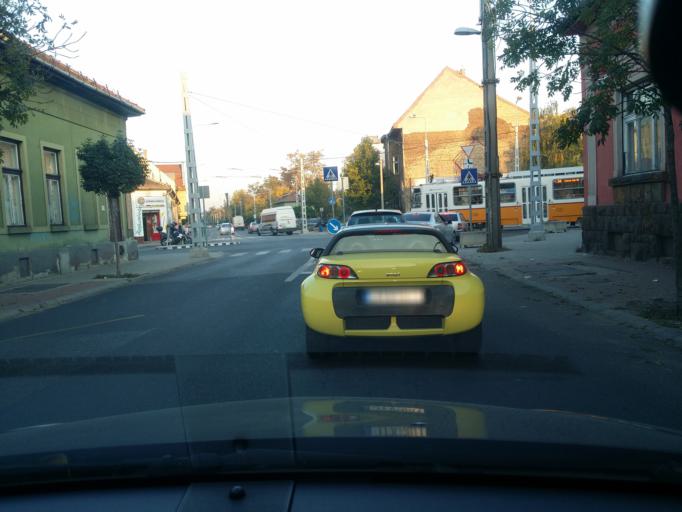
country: HU
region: Budapest
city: Budapest IV. keruelet
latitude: 47.5650
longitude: 19.0907
